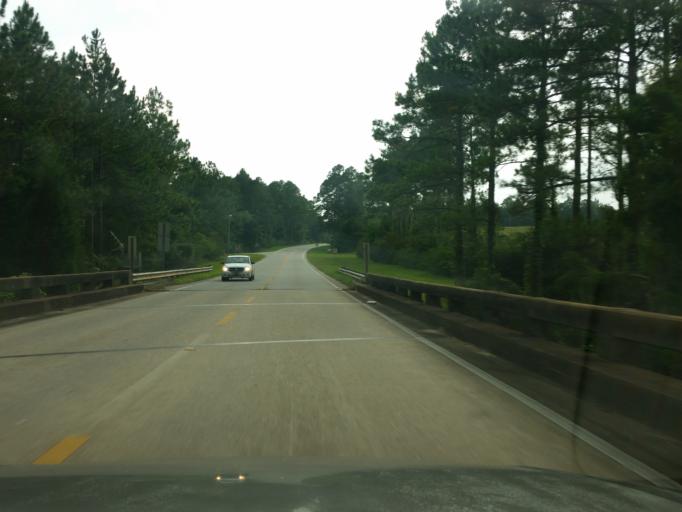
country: US
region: Florida
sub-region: Escambia County
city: Cantonment
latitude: 30.5183
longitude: -87.4634
